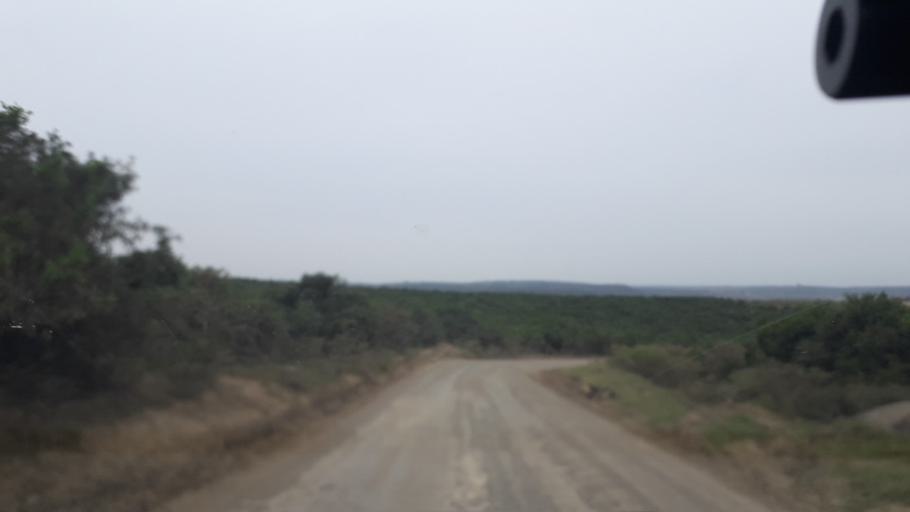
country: ZA
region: Eastern Cape
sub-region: Buffalo City Metropolitan Municipality
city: Bhisho
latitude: -32.7923
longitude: 27.3410
